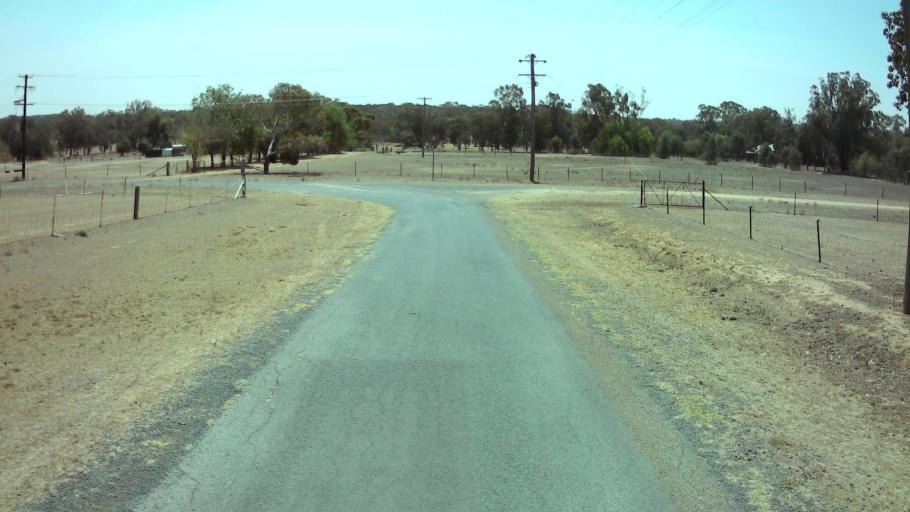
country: AU
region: New South Wales
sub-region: Weddin
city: Grenfell
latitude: -33.8924
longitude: 148.1723
